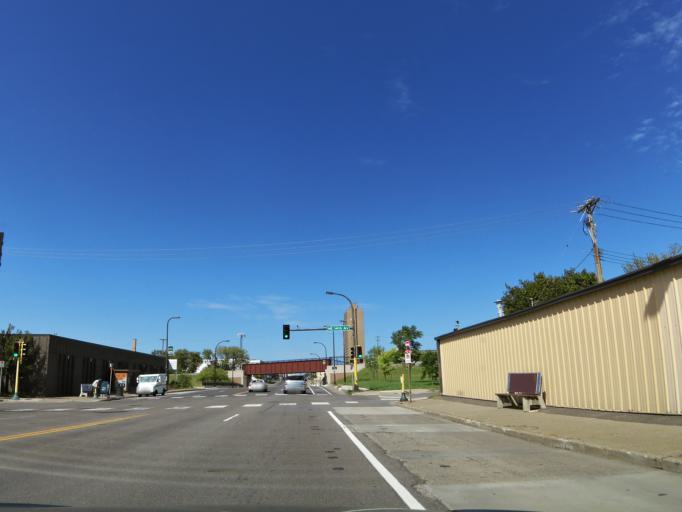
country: US
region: Minnesota
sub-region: Hennepin County
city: Minneapolis
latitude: 45.0020
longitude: -93.2473
